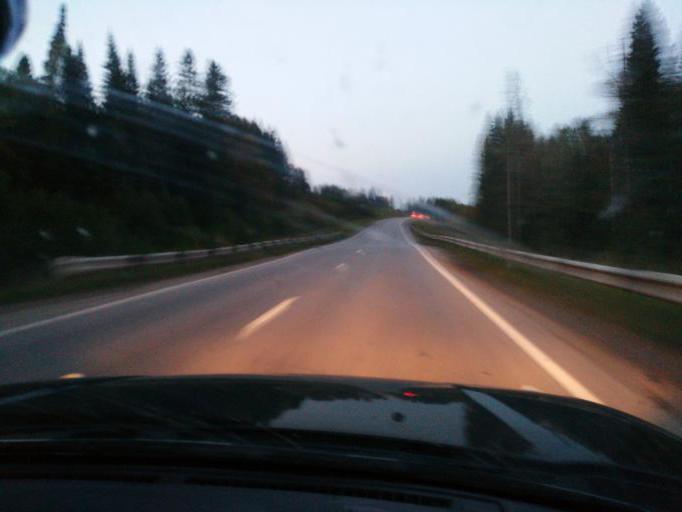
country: RU
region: Perm
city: Kalino
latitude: 58.2772
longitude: 57.3958
